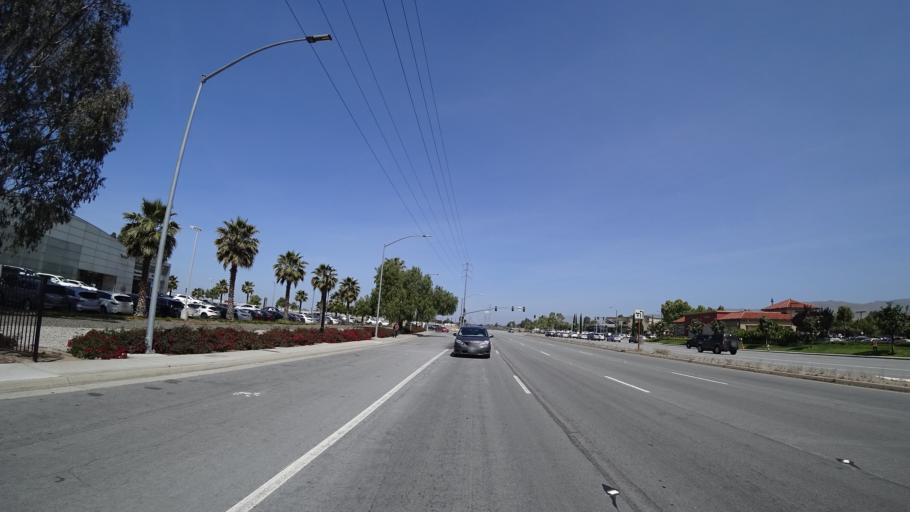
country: US
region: California
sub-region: Santa Clara County
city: Alum Rock
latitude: 37.3302
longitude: -121.8123
